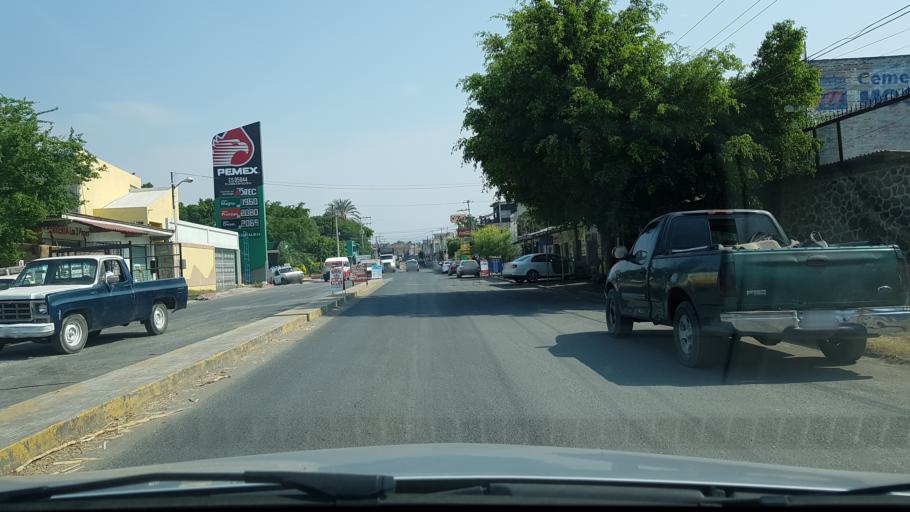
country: MX
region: Morelos
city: Zacatepec
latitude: 18.6668
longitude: -99.1861
